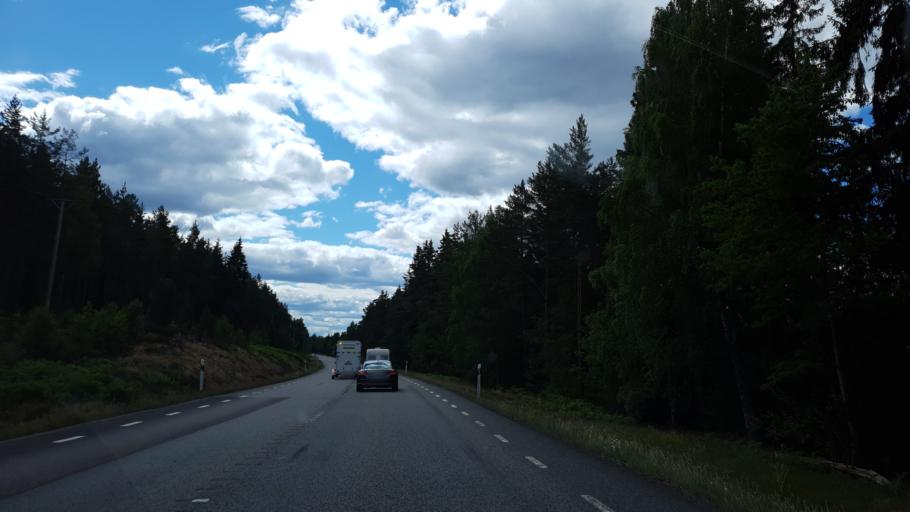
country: SE
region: Kronoberg
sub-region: Vaxjo Kommun
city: Braas
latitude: 57.1523
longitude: 15.1593
